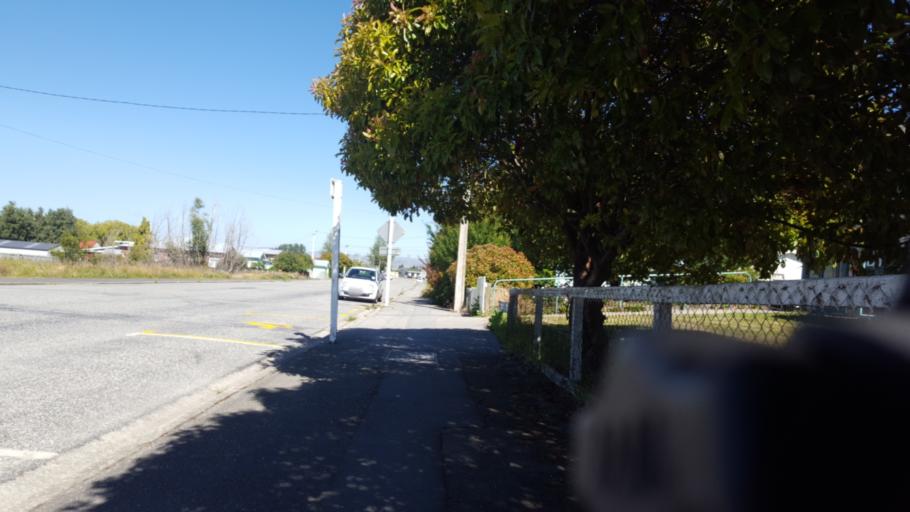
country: NZ
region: Otago
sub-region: Dunedin City
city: Dunedin
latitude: -45.1256
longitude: 170.0986
